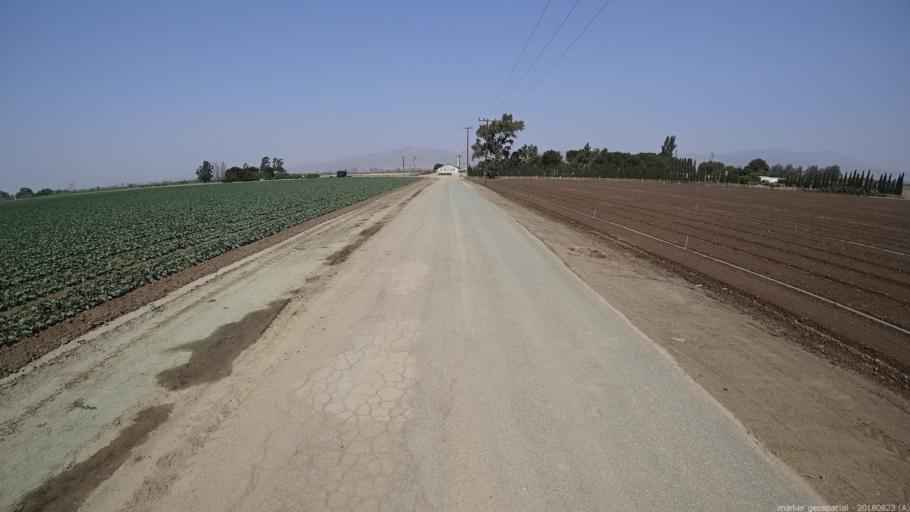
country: US
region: California
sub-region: Monterey County
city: Soledad
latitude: 36.4084
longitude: -121.3483
